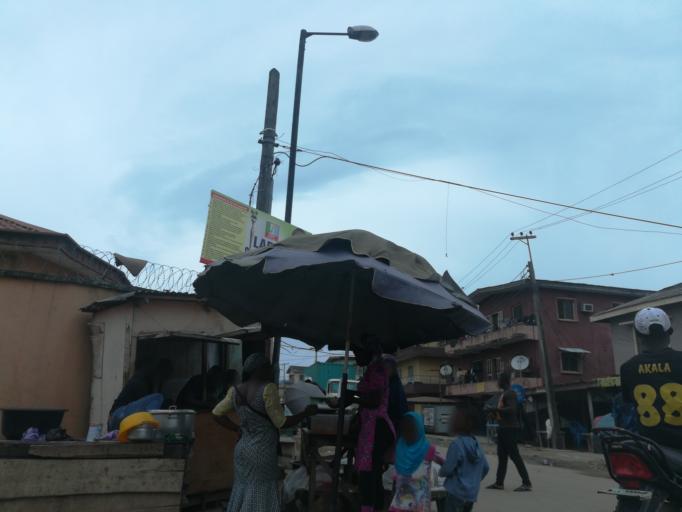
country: NG
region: Lagos
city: Ebute Metta
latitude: 6.4898
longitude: 3.3880
